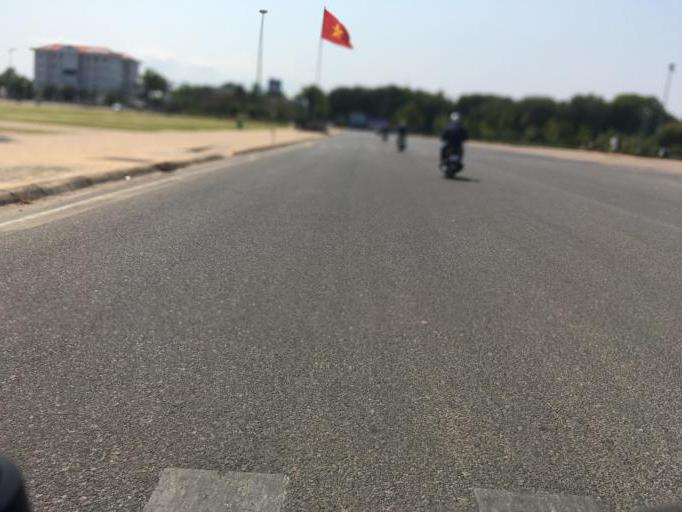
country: VN
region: Ninh Thuan
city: Phan Rang-Thap Cham
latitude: 11.5655
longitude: 109.0005
